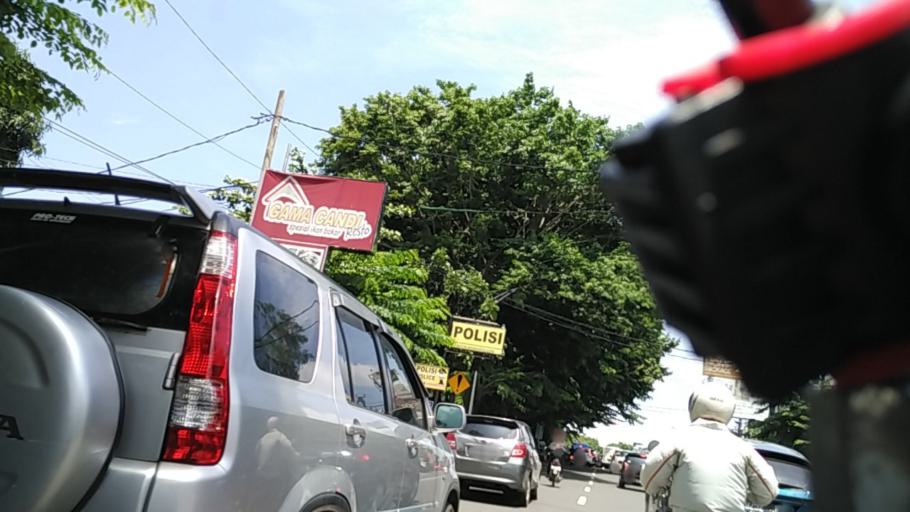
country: ID
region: Central Java
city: Semarang
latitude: -7.0170
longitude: 110.4187
